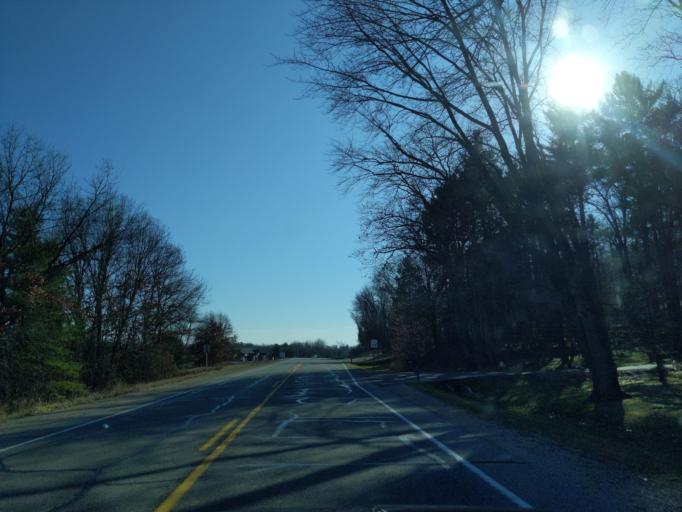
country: US
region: Wisconsin
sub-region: Waushara County
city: Wautoma
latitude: 44.0866
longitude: -89.2911
